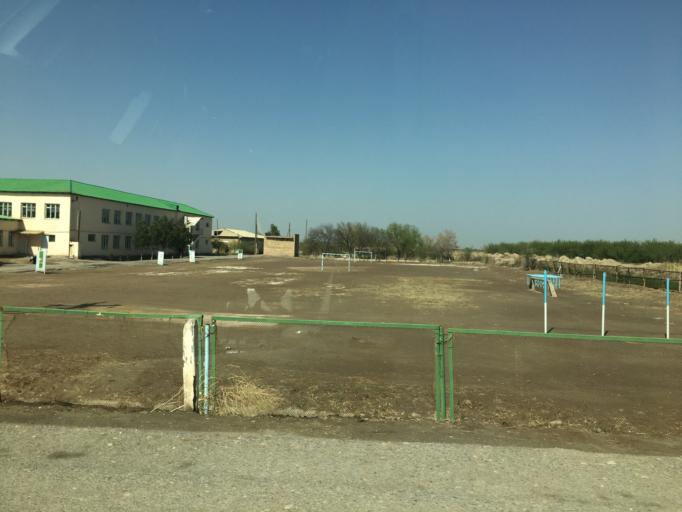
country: TM
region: Lebap
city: Turkmenabat
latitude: 38.9658
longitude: 63.6530
